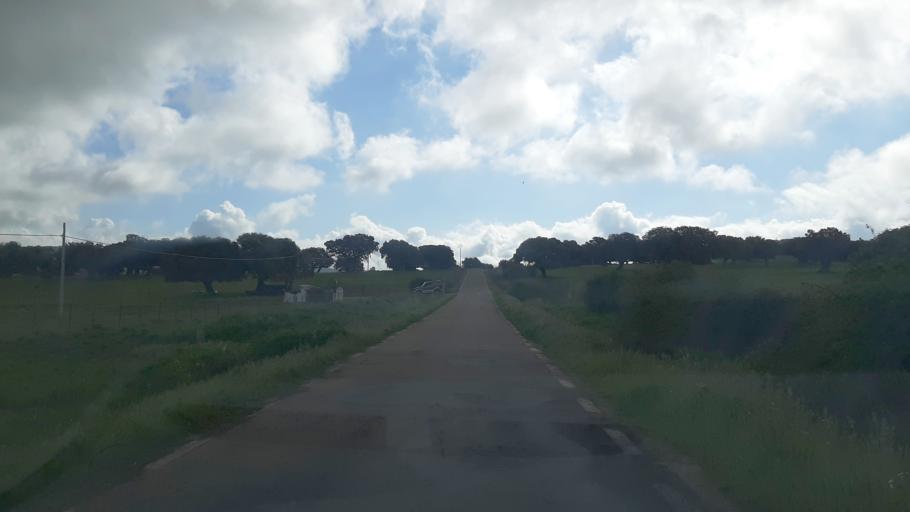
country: ES
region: Castille and Leon
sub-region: Provincia de Salamanca
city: Narros de Matalayegua
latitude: 40.7030
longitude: -5.9177
